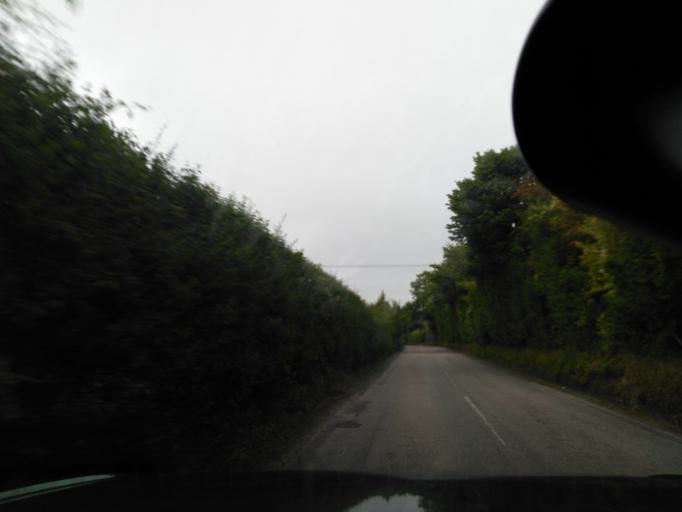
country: GB
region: England
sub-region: Dorset
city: Blandford Forum
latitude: 50.9229
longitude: -2.1941
